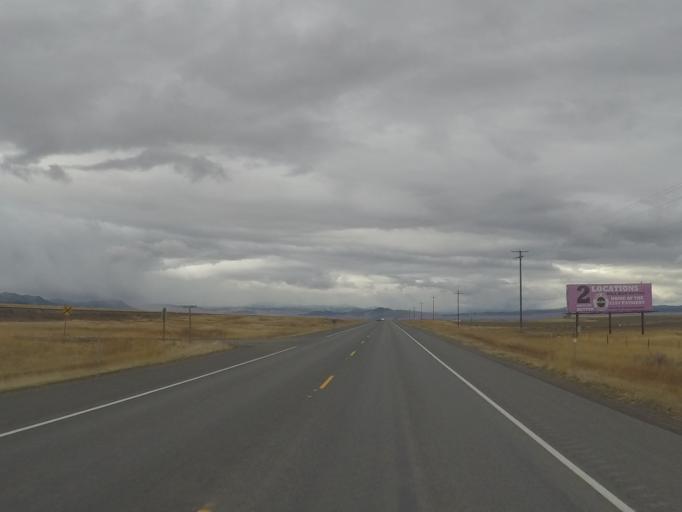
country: US
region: Montana
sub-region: Lewis and Clark County
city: East Helena
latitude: 46.5732
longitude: -111.8285
